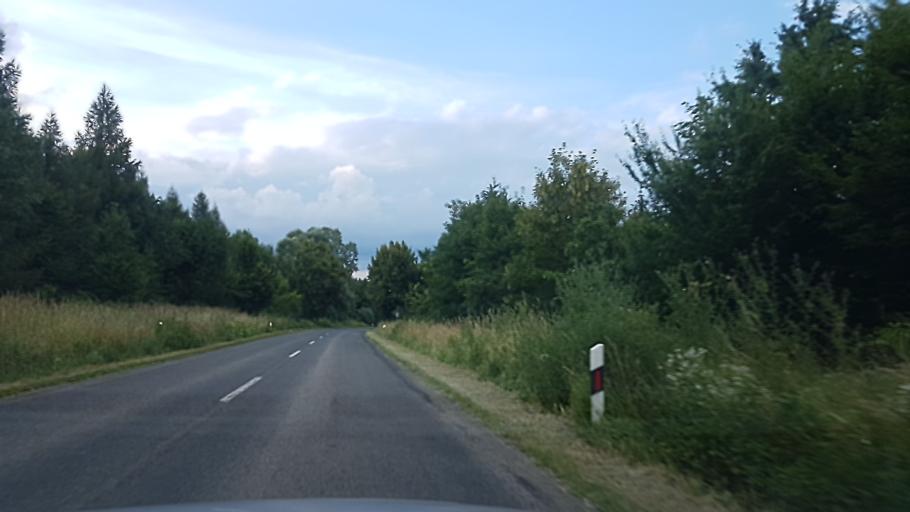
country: HU
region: Somogy
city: Kaposvar
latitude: 46.2628
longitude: 17.8264
